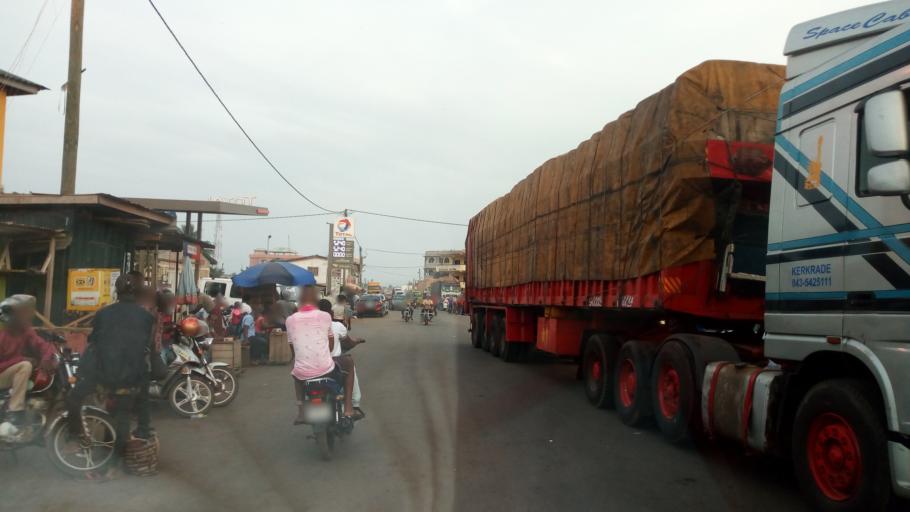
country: TG
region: Maritime
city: Lome
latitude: 6.1134
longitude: 1.1953
